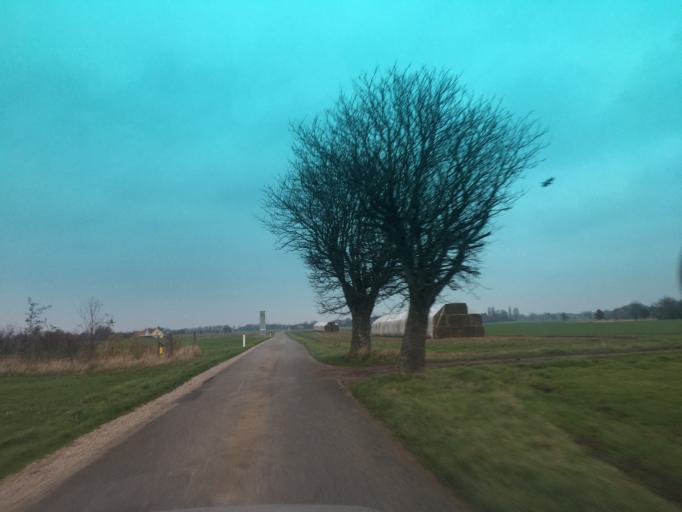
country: DK
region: Zealand
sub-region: Naestved Kommune
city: Fuglebjerg
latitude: 55.2724
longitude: 11.4243
